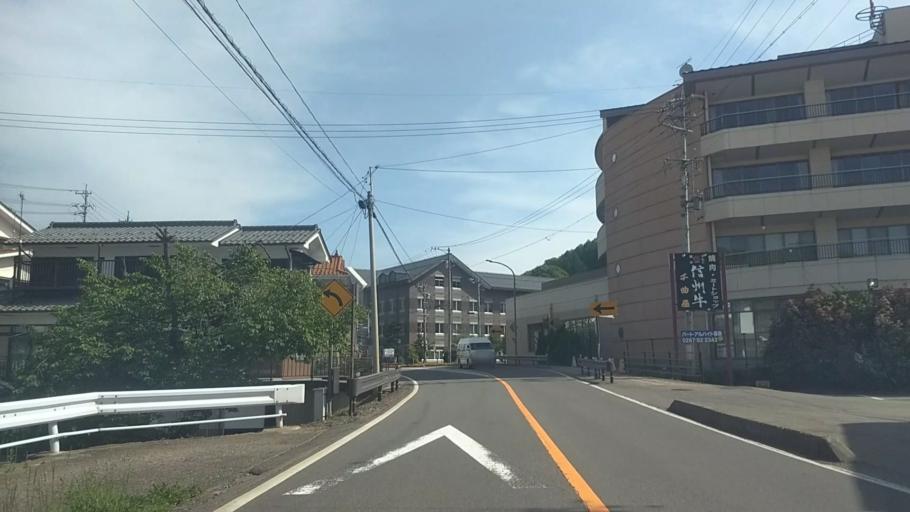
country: JP
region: Nagano
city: Saku
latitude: 36.0936
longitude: 138.4832
